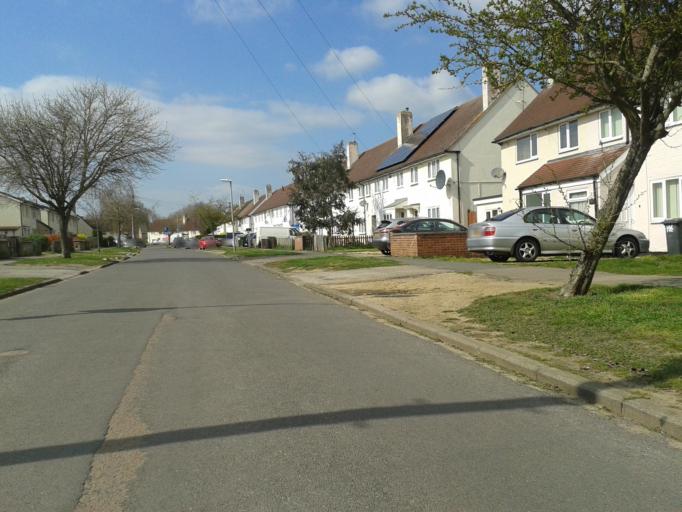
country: GB
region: England
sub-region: Cambridgeshire
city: Cambridge
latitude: 52.1747
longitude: 0.1181
